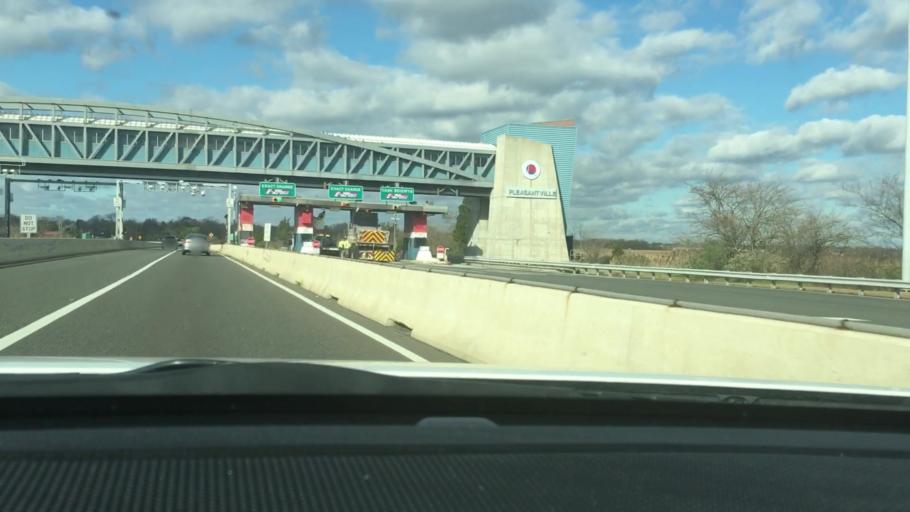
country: US
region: New Jersey
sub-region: Atlantic County
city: Pleasantville
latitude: 39.3912
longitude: -74.5100
